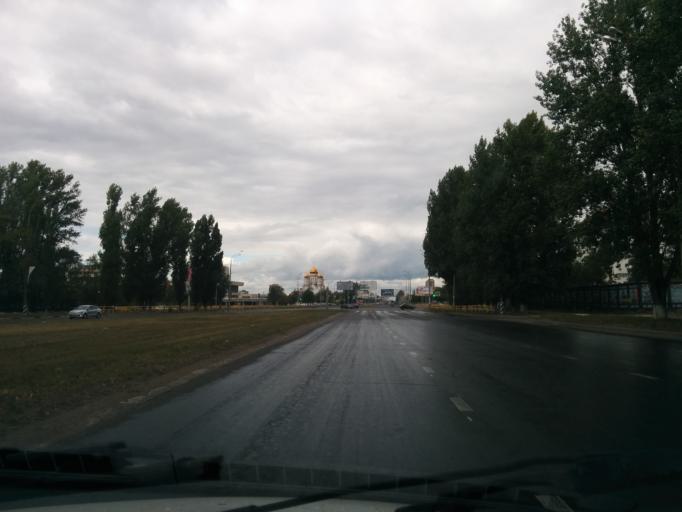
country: RU
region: Samara
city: Tol'yatti
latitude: 53.5134
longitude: 49.2781
